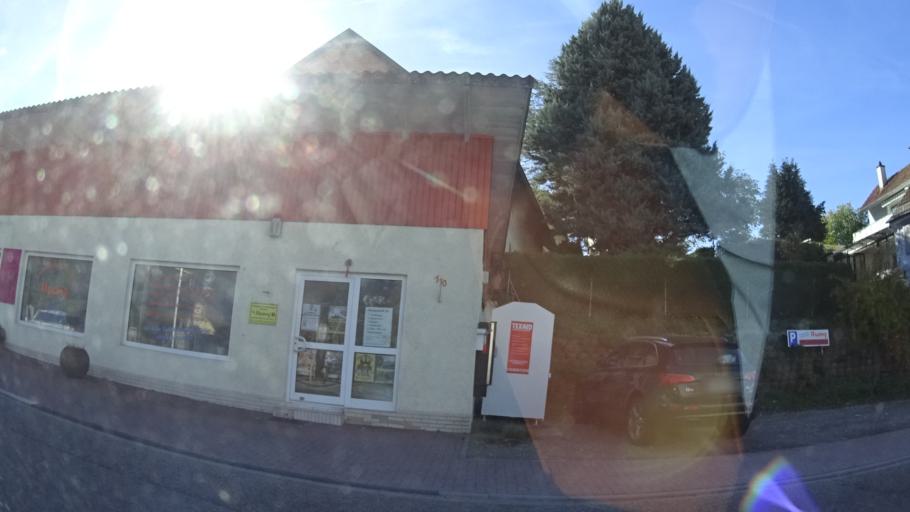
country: DE
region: Baden-Wuerttemberg
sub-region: Karlsruhe Region
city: Joehlingen
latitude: 48.9851
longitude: 8.5448
